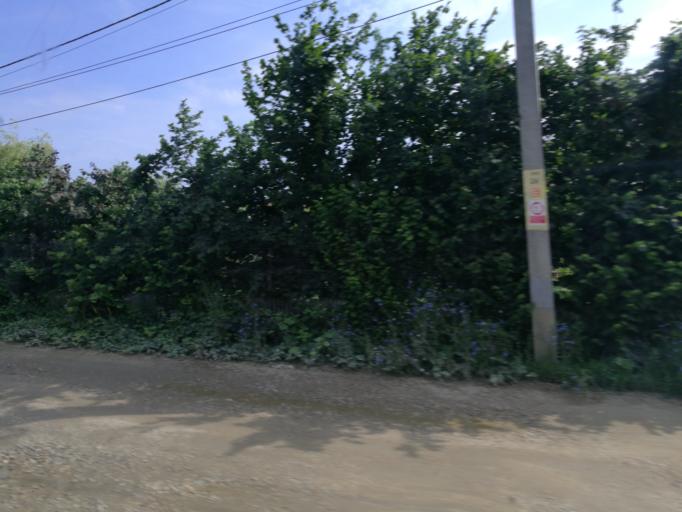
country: RO
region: Arges
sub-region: Comuna Bradu
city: Geamana
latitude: 44.8324
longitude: 24.9141
